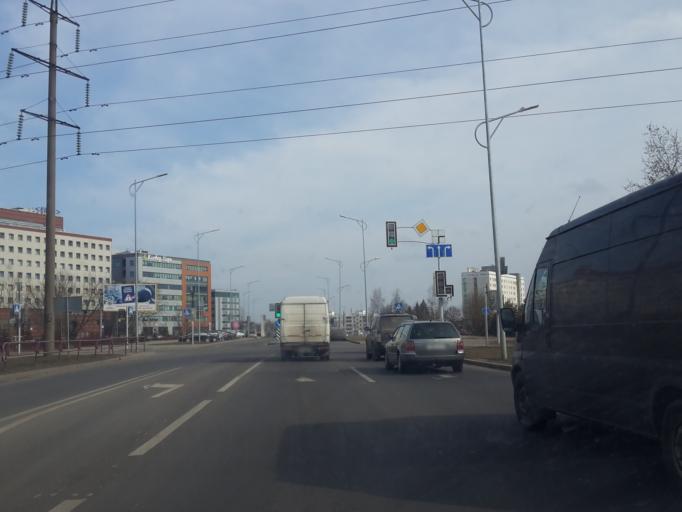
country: BY
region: Minsk
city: Borovlyany
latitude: 53.9253
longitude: 27.6804
